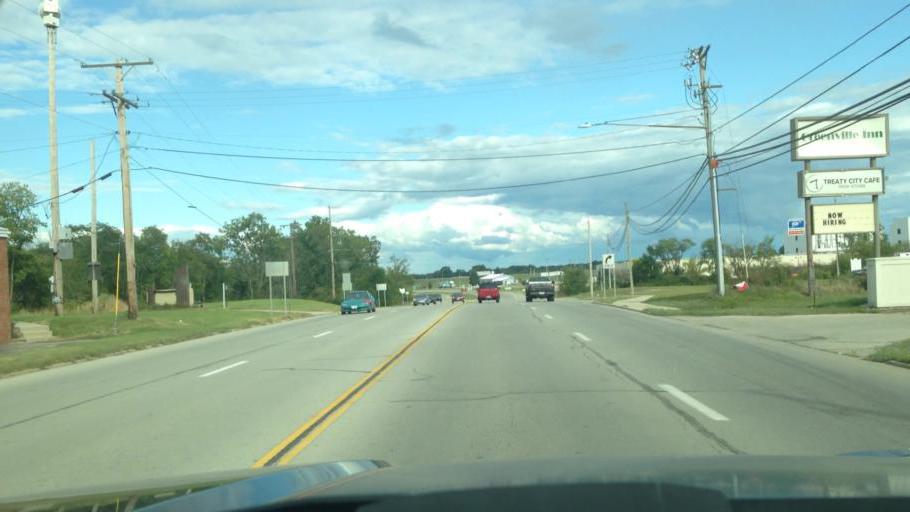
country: US
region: Ohio
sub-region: Darke County
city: Greenville
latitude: 40.0987
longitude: -84.6162
